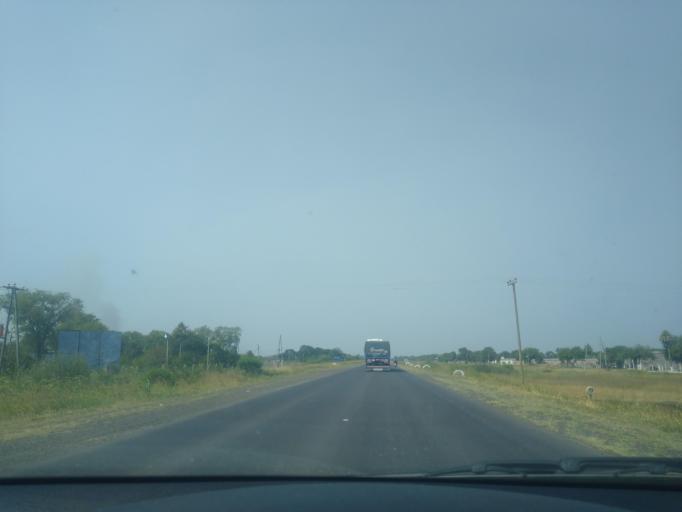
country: AR
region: Chaco
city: Fontana
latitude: -27.4836
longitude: -59.0654
